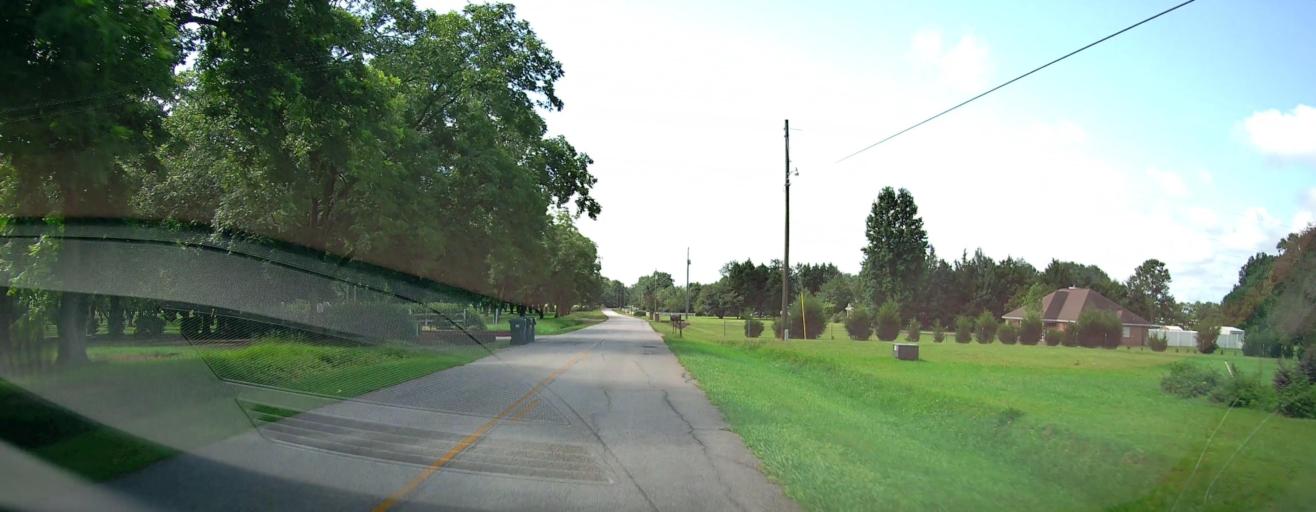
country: US
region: Georgia
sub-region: Peach County
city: Byron
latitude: 32.6562
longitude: -83.7814
